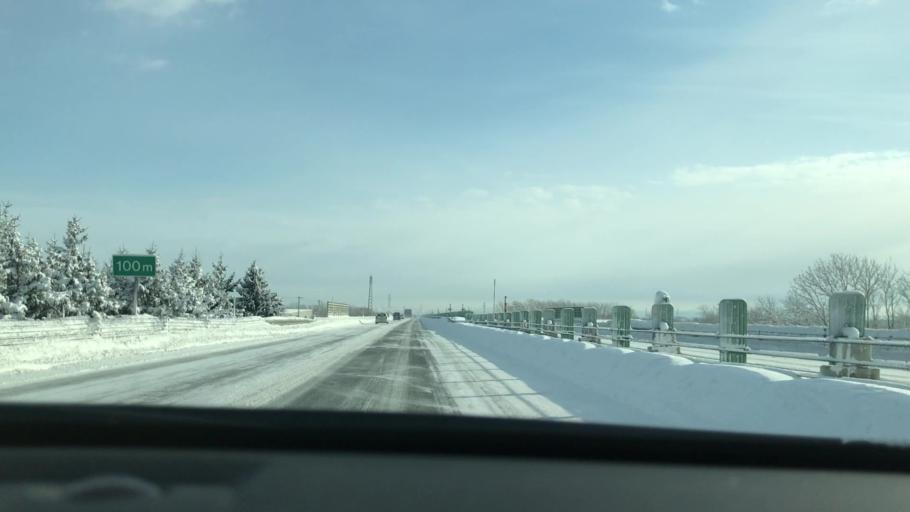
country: JP
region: Hokkaido
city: Ebetsu
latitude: 43.0872
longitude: 141.4511
